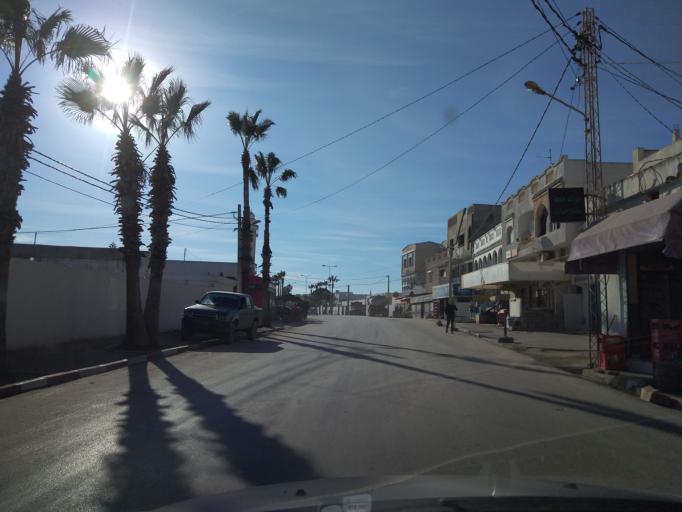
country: TN
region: Ariana
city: Qal'at al Andalus
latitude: 37.0602
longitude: 10.1127
